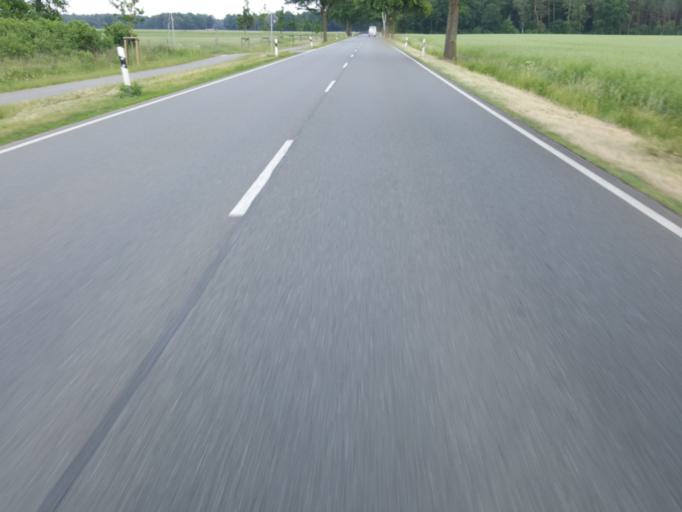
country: DE
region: Lower Saxony
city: Leese
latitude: 52.4874
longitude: 9.1289
